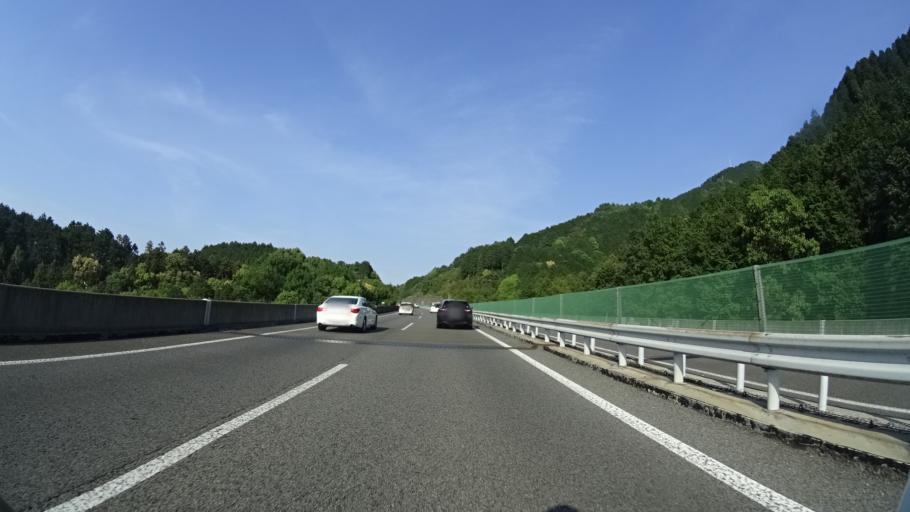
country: JP
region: Ehime
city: Niihama
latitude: 33.9101
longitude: 133.2643
